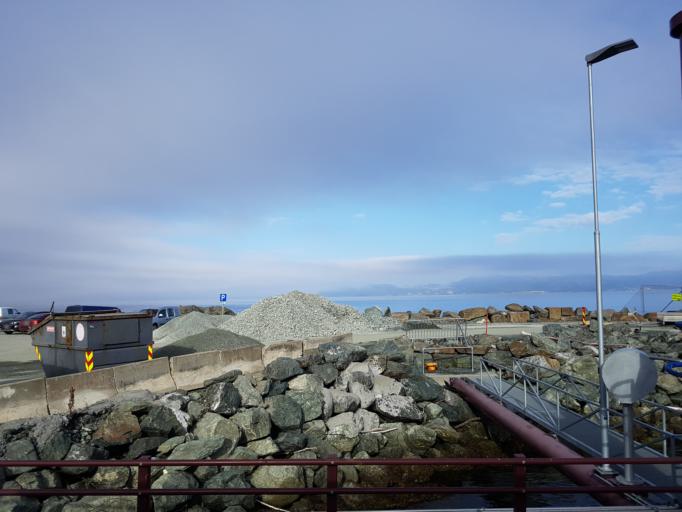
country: NO
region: Sor-Trondelag
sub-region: Skaun
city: Borsa
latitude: 63.4513
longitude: 10.2010
